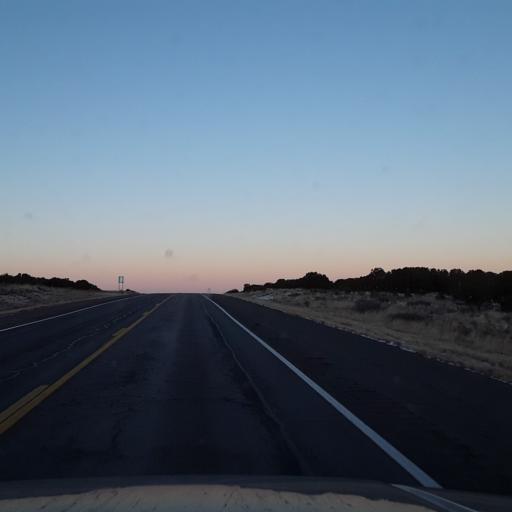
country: US
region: New Mexico
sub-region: Torrance County
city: Estancia
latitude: 34.5194
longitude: -105.3339
